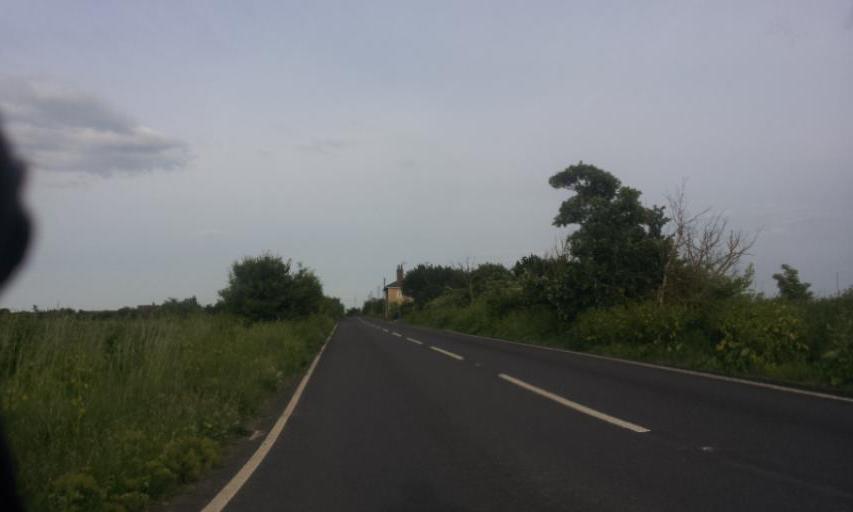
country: GB
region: England
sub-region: Kent
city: Queenborough
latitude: 51.4097
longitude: 0.7652
